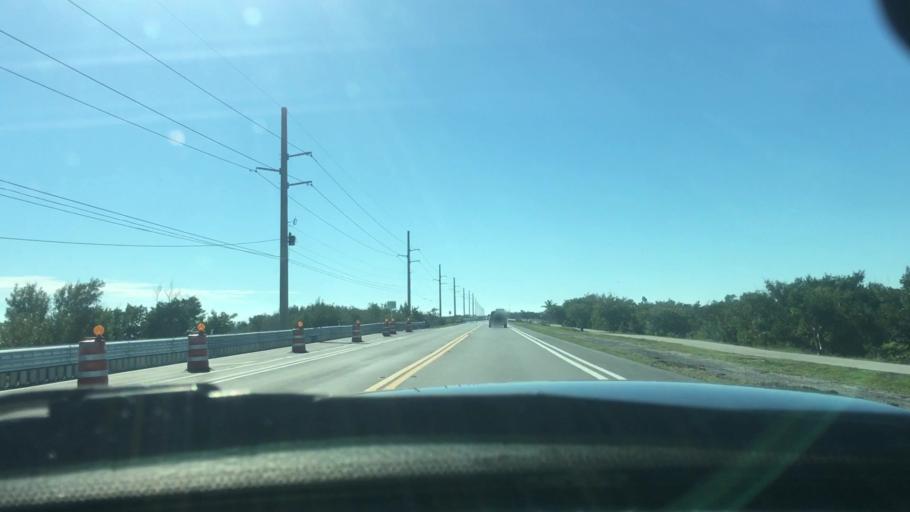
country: US
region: Florida
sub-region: Monroe County
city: Big Pine Key
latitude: 24.6810
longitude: -81.2316
